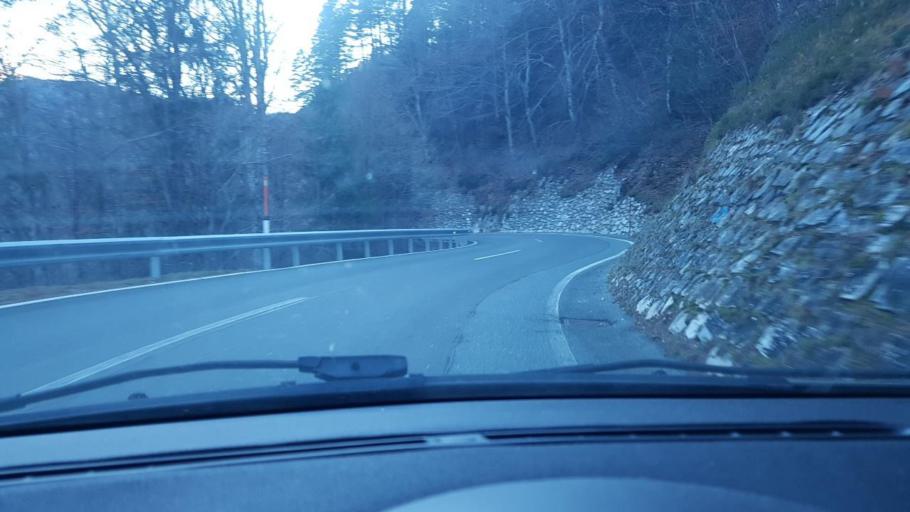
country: AT
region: Carinthia
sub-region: Politischer Bezirk Klagenfurt Land
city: Ferlach
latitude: 46.4894
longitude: 14.2756
